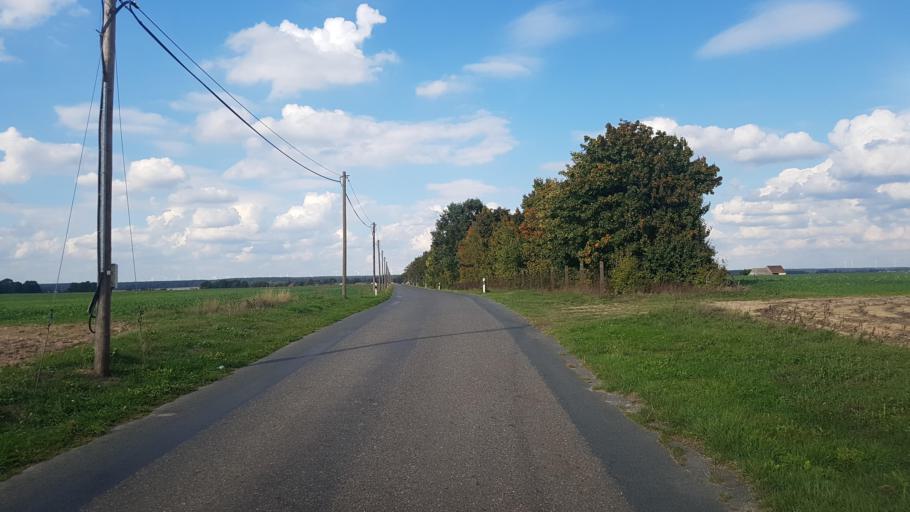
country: DE
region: Brandenburg
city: Dahme
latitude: 51.8750
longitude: 13.3832
